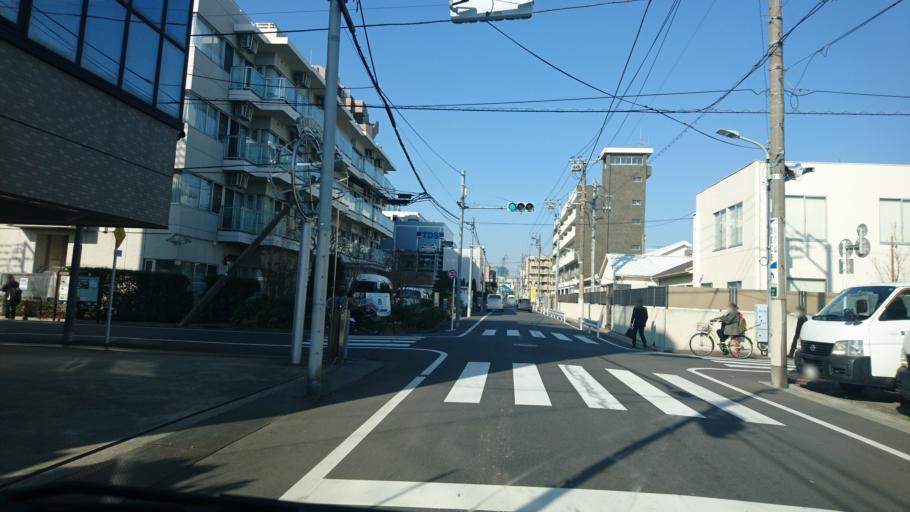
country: JP
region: Kanagawa
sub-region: Kawasaki-shi
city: Kawasaki
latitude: 35.5595
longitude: 139.7004
